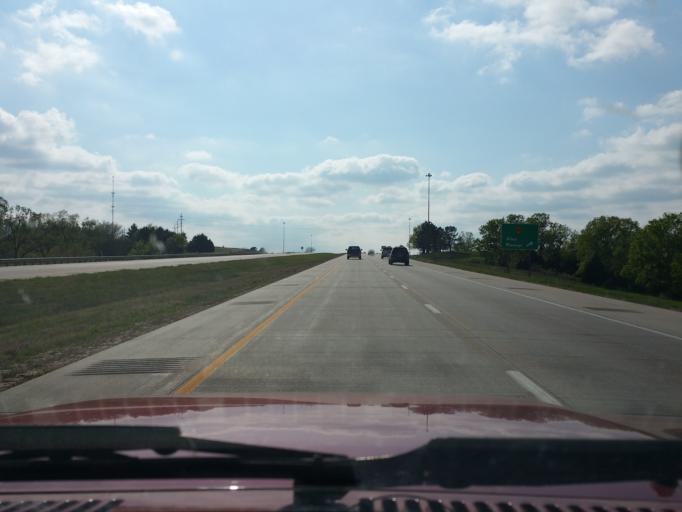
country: US
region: Kansas
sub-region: Wabaunsee County
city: Alma
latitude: 39.0658
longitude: -96.2824
